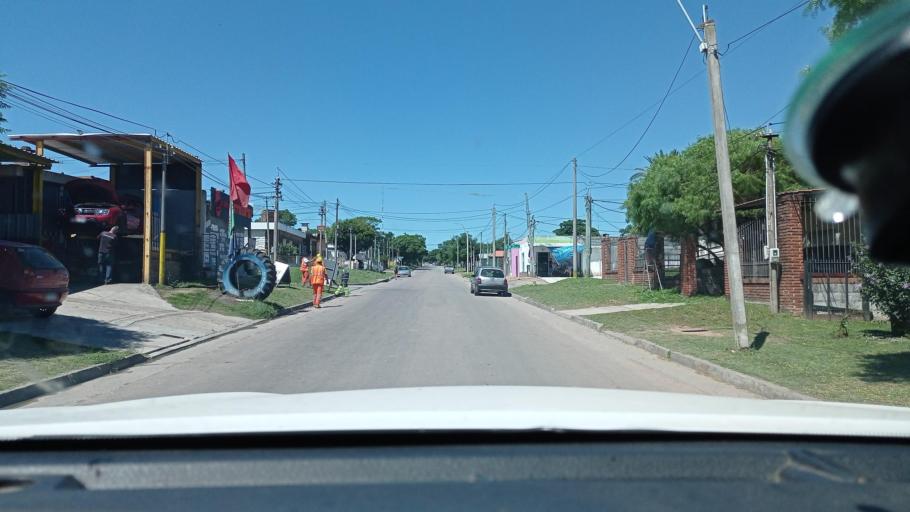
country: UY
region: Canelones
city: Las Piedras
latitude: -34.7364
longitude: -56.2203
